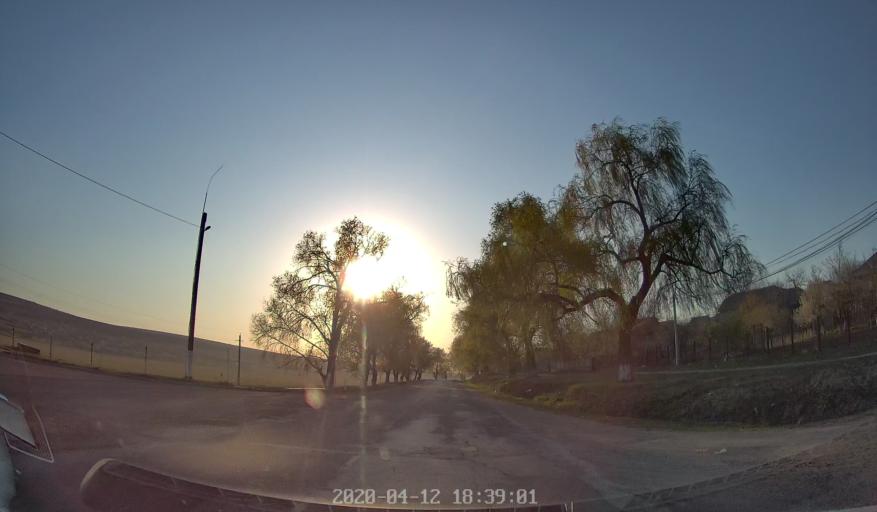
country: MD
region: Chisinau
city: Vadul lui Voda
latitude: 47.1266
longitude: 28.9928
